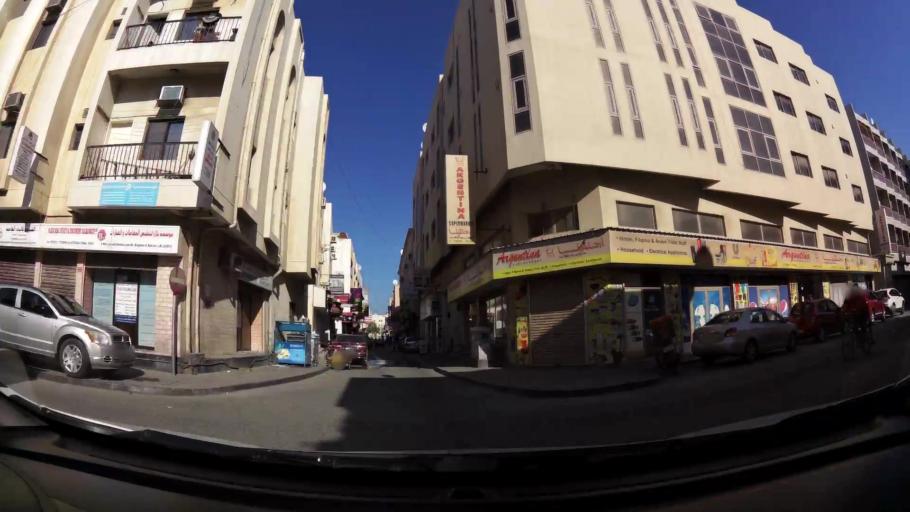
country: BH
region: Manama
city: Manama
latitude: 26.2271
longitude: 50.5841
